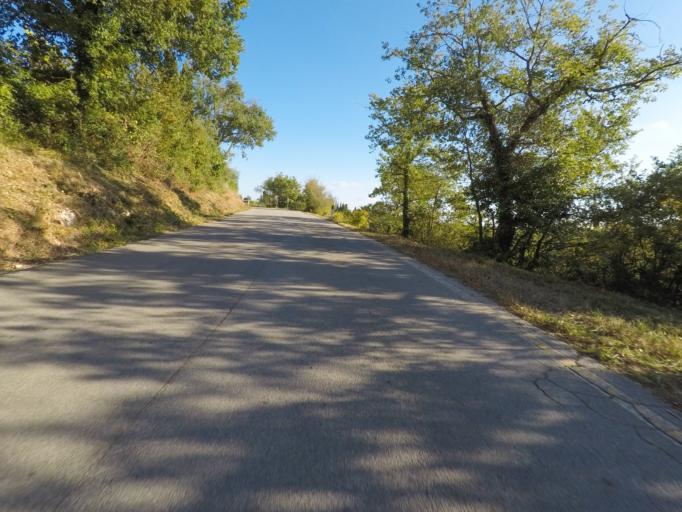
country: IT
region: Tuscany
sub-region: Provincia di Siena
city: Radda in Chianti
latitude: 43.4523
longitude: 11.3861
